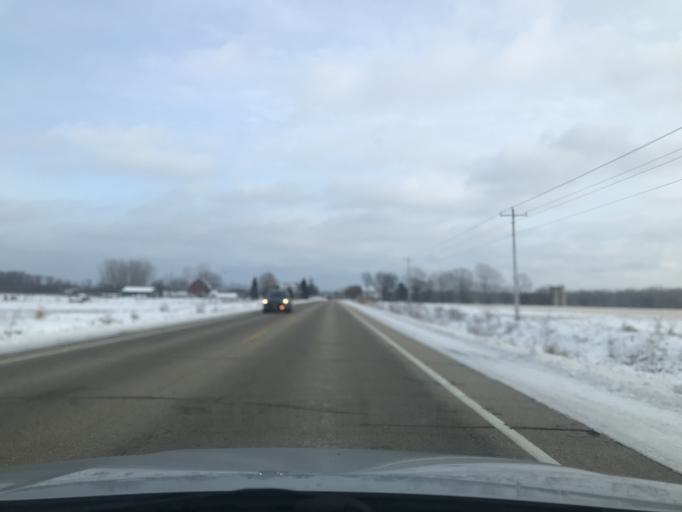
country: US
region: Wisconsin
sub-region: Oconto County
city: Oconto
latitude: 44.8924
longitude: -87.9316
